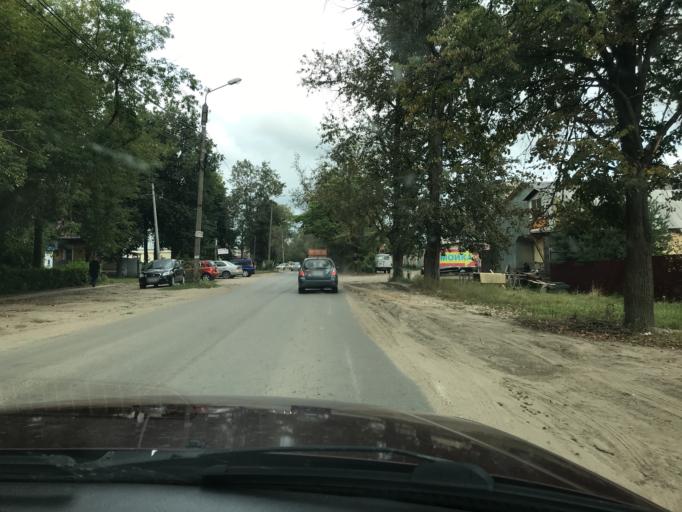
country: RU
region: Kaluga
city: Maloyaroslavets
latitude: 55.0029
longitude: 36.4717
